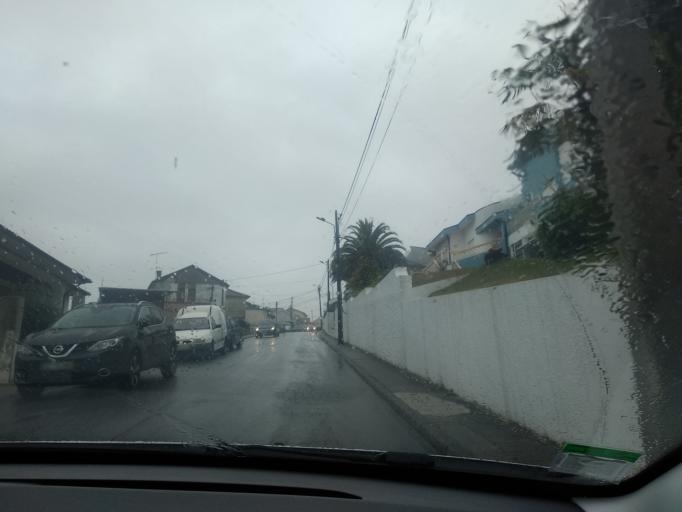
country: PT
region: Braga
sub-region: Braga
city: Braga
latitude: 41.5621
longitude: -8.4039
